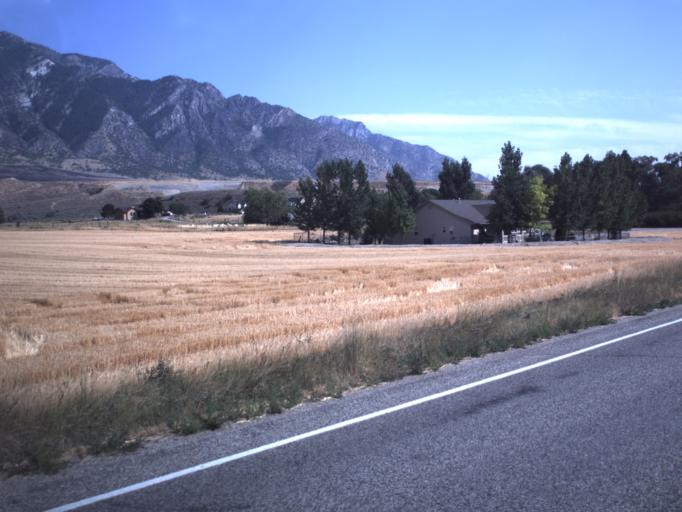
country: US
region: Utah
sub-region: Box Elder County
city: Honeyville
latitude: 41.6727
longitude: -112.0898
